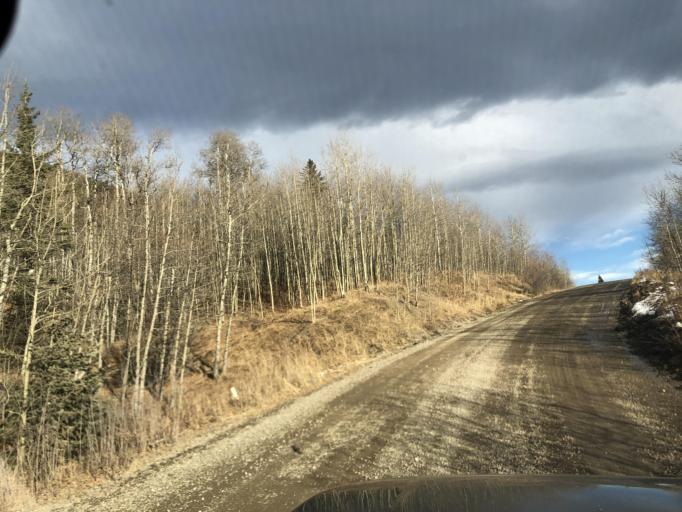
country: CA
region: Alberta
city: Cochrane
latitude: 51.0229
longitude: -114.8962
